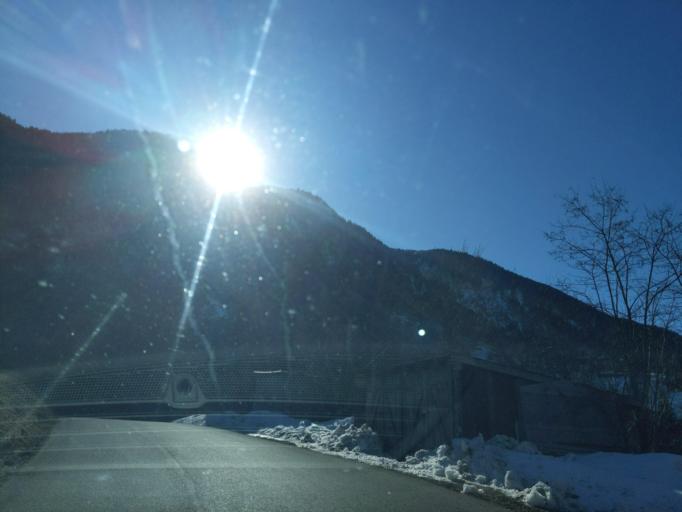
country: FR
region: Rhone-Alpes
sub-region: Departement de la Savoie
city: Salins-les-Thermes
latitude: 45.4361
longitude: 6.5020
